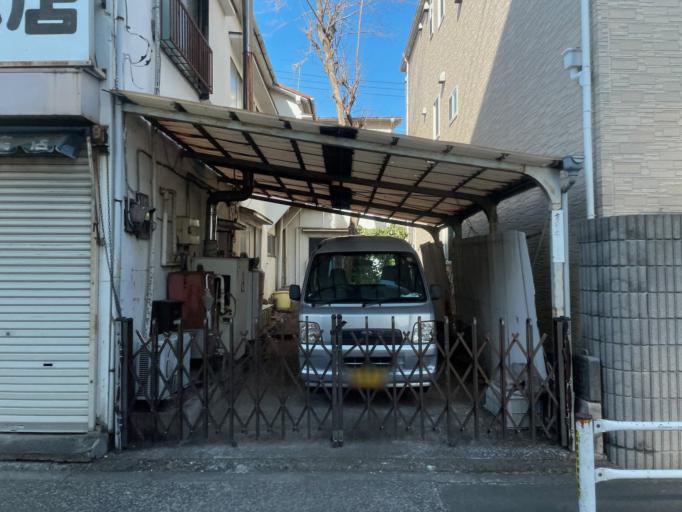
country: JP
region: Tokyo
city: Tanashicho
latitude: 35.7465
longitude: 139.5304
